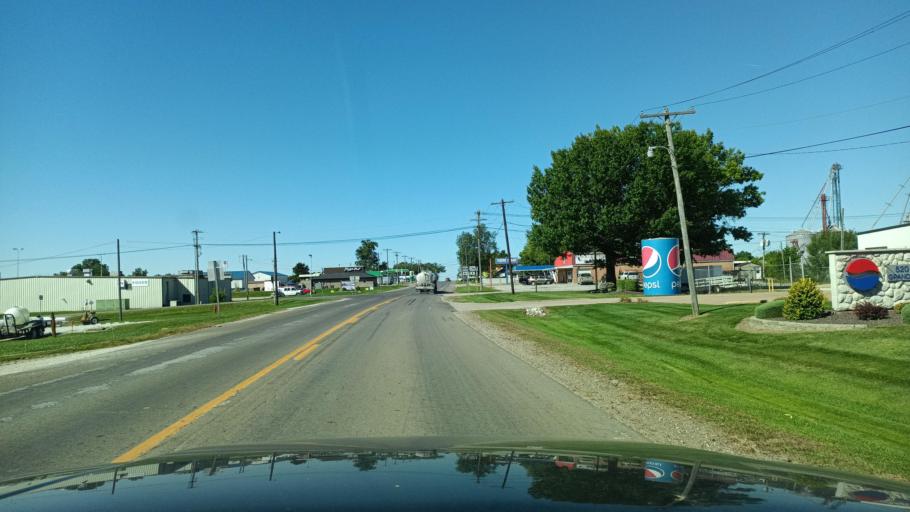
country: US
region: Missouri
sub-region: Scotland County
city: Memphis
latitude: 40.4514
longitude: -92.1618
